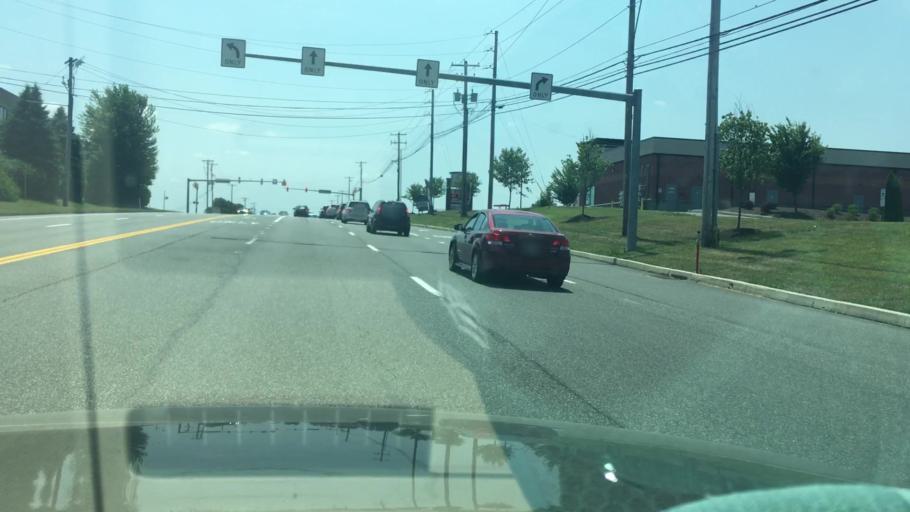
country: US
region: Pennsylvania
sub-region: Lehigh County
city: Trexlertown
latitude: 40.5919
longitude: -75.6297
